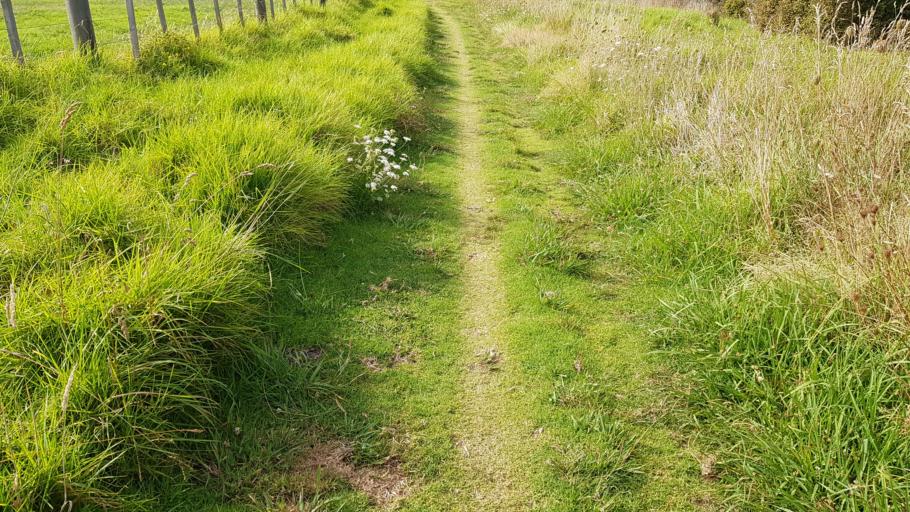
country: NZ
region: Auckland
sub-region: Auckland
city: Rothesay Bay
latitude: -36.6638
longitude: 174.7463
